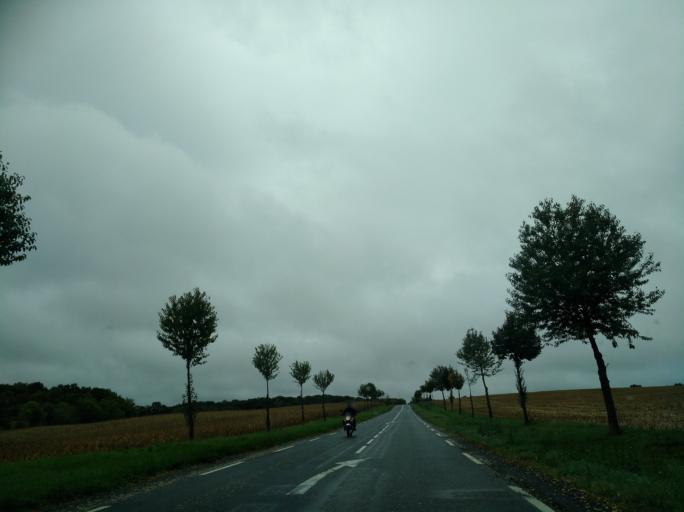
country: FR
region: Rhone-Alpes
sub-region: Departement de l'Ain
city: Saint-Trivier-sur-Moignans
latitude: 46.1066
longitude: 4.8880
